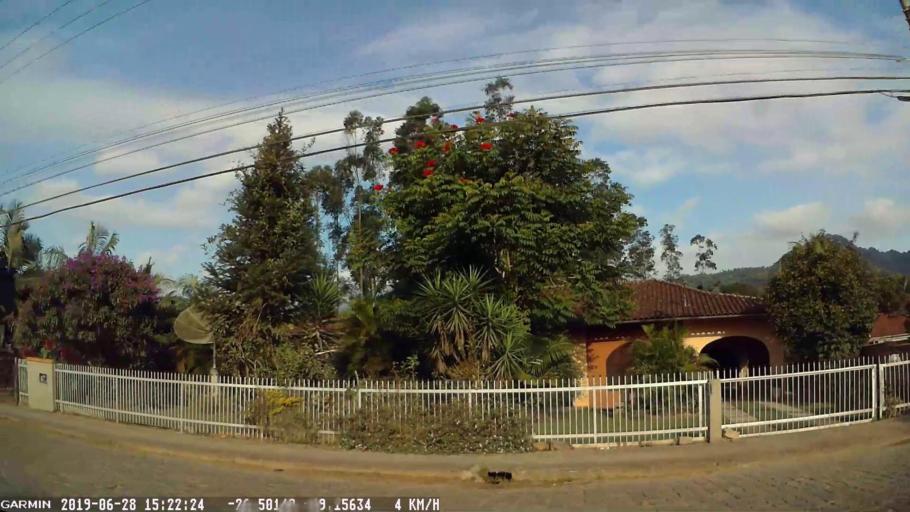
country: BR
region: Santa Catarina
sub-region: Jaragua Do Sul
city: Jaragua do Sul
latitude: -26.5015
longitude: -49.1565
